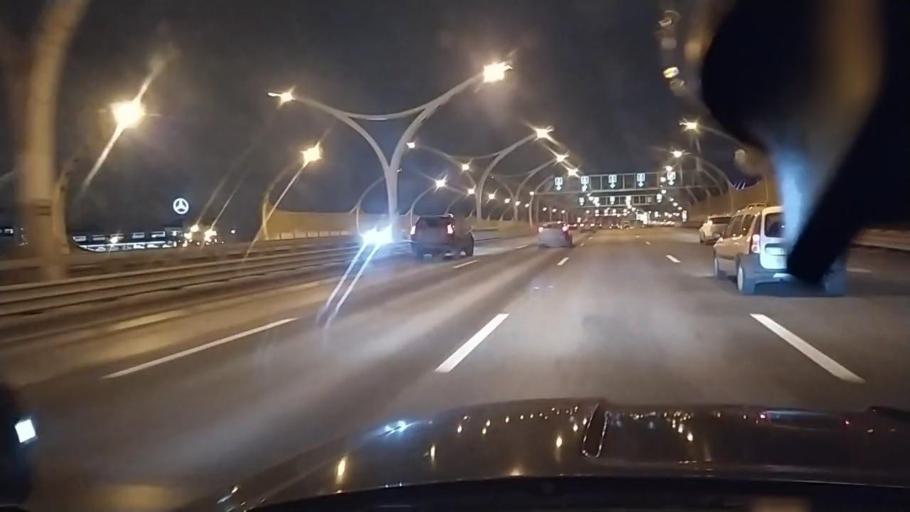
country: RU
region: St.-Petersburg
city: Staraya Derevnya
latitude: 59.9866
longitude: 30.2301
